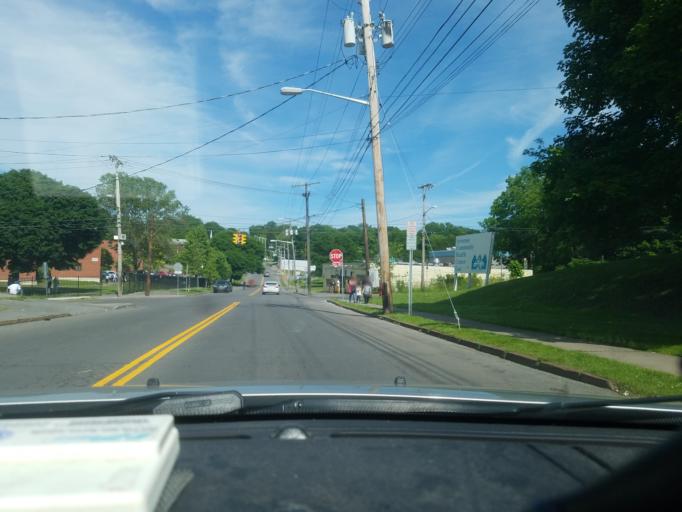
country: US
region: New York
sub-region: Onondaga County
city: Syracuse
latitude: 43.0481
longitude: -76.1153
